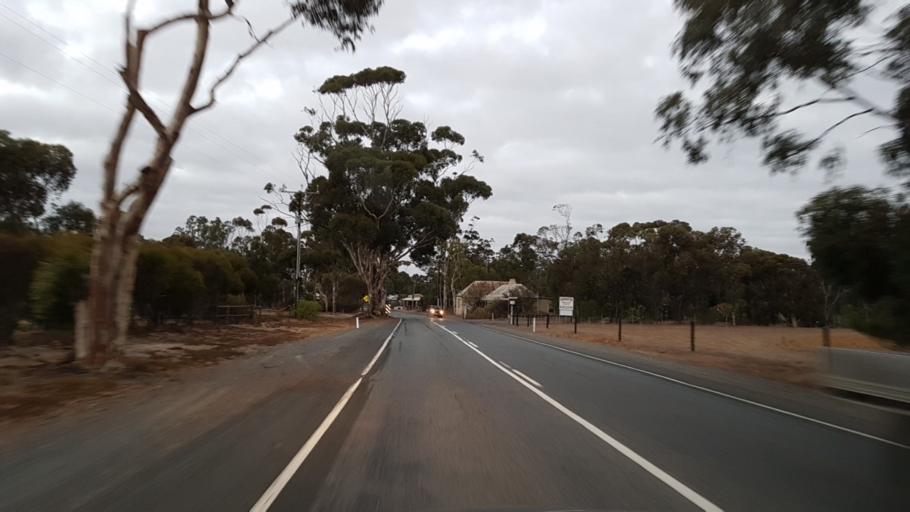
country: AU
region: South Australia
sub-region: Mount Barker
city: Callington
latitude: -35.0669
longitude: 139.0127
